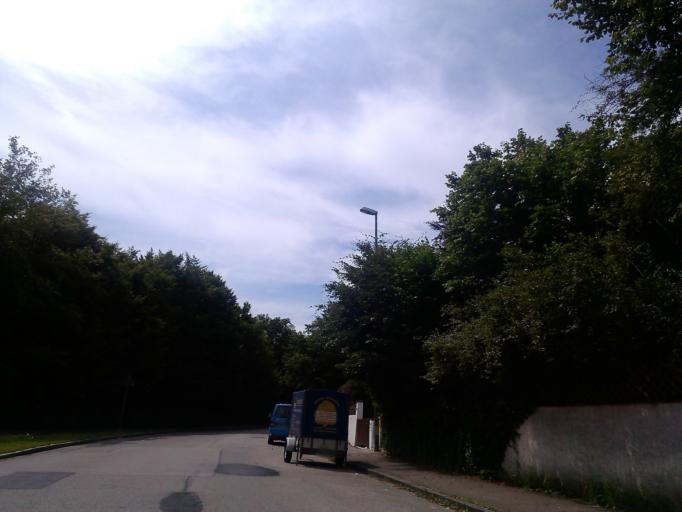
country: DE
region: Bavaria
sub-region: Upper Bavaria
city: Gauting
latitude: 48.0763
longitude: 11.3783
